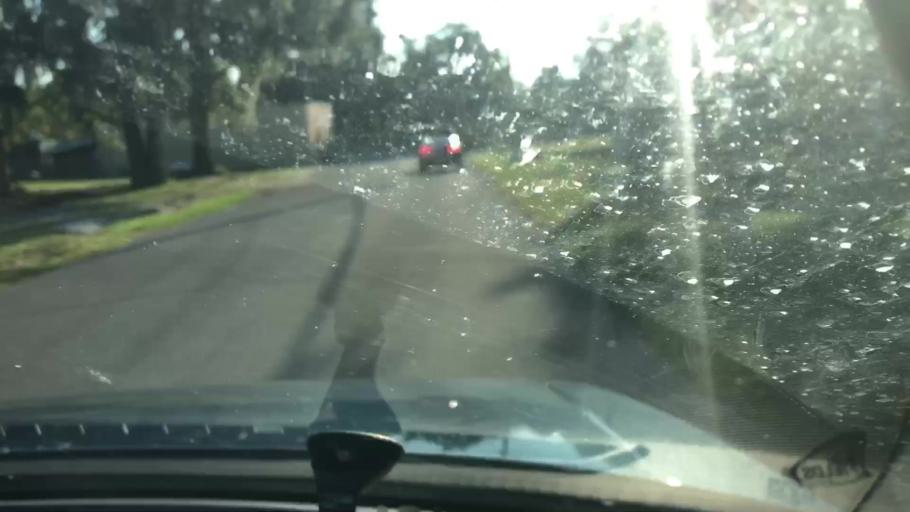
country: US
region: Florida
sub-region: Polk County
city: Kathleen
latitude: 28.1229
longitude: -82.0258
